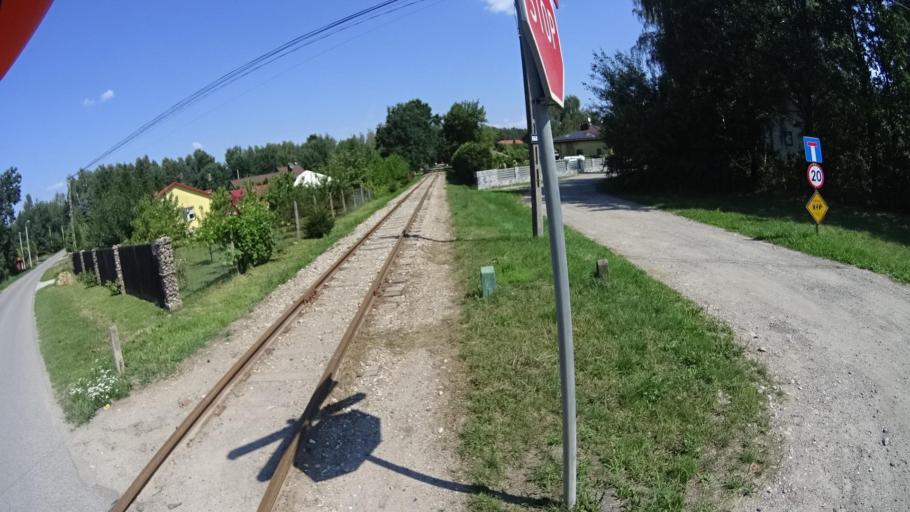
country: PL
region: Masovian Voivodeship
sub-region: Powiat piaseczynski
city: Tarczyn
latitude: 51.9914
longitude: 20.8902
